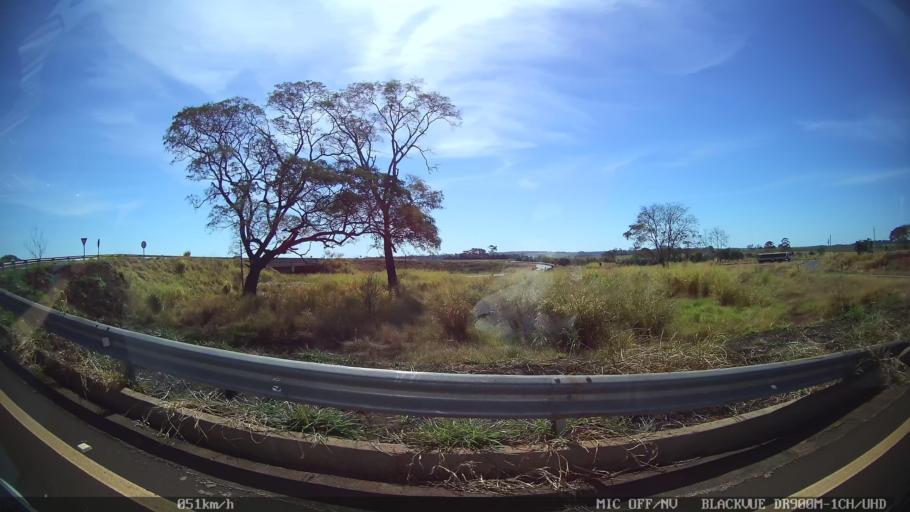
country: BR
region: Sao Paulo
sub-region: Nuporanga
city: Nuporanga
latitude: -20.5623
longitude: -47.6244
